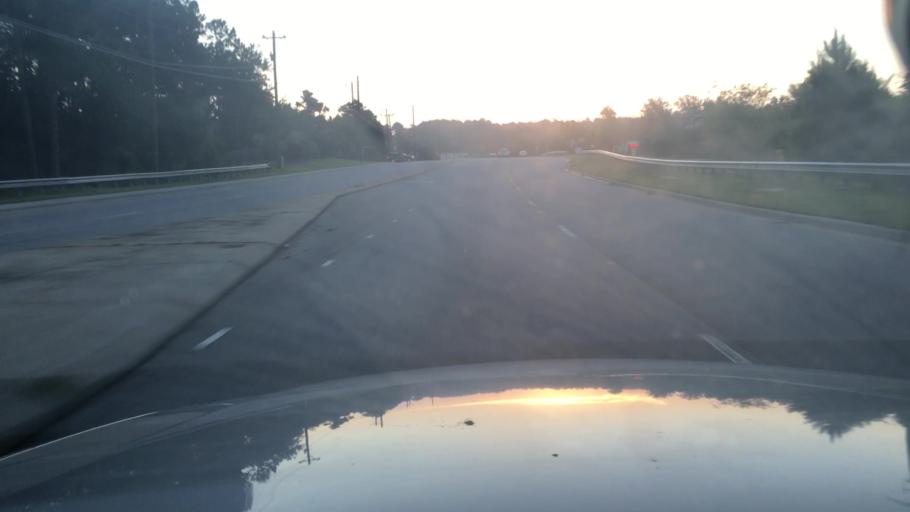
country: US
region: North Carolina
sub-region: Hoke County
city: Rockfish
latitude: 35.0620
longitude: -79.0419
